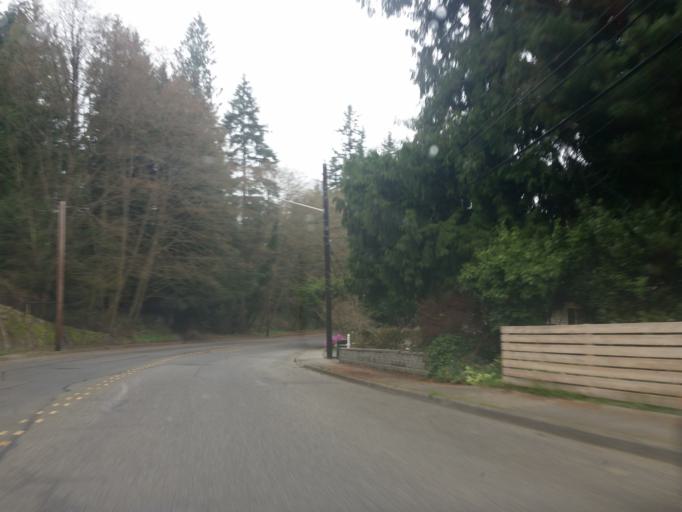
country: US
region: Washington
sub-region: Snohomish County
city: Lynnwood
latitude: 47.8268
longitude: -122.3368
